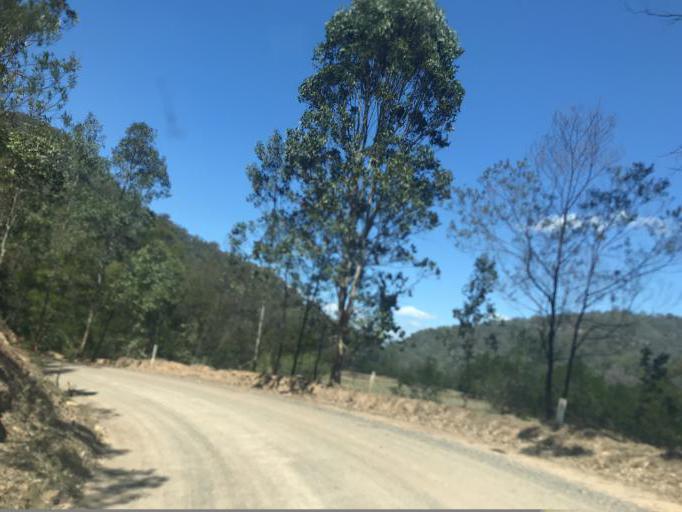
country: AU
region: New South Wales
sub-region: Hornsby Shire
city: Glenorie
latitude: -33.2112
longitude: 150.9783
